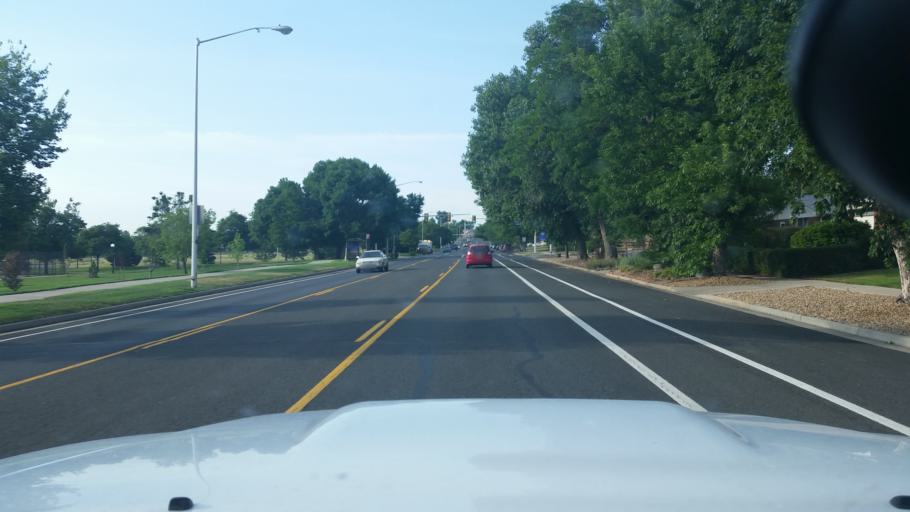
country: US
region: Colorado
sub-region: Broomfield County
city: Broomfield
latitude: 39.9194
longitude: -105.0719
